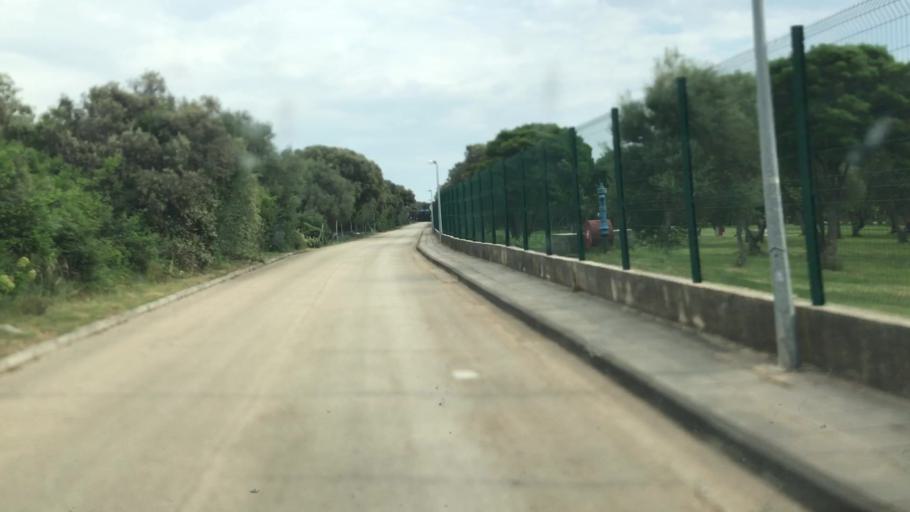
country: HR
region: Licko-Senjska
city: Novalja
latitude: 44.5425
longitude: 14.8843
